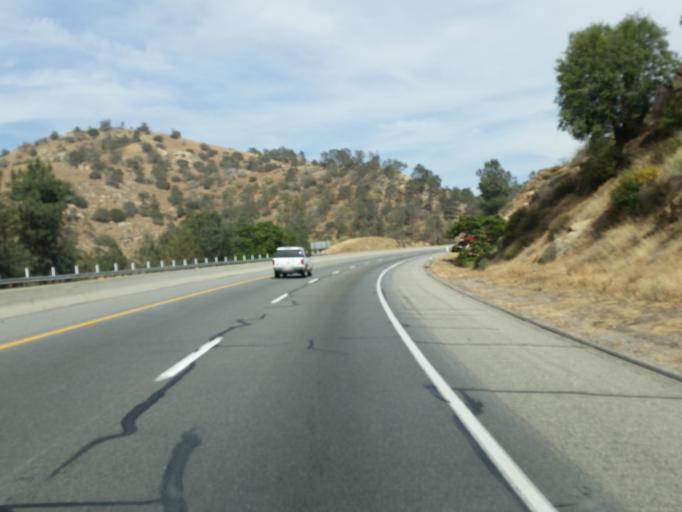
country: US
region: California
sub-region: Kern County
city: Bear Valley Springs
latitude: 35.2224
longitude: -118.5607
